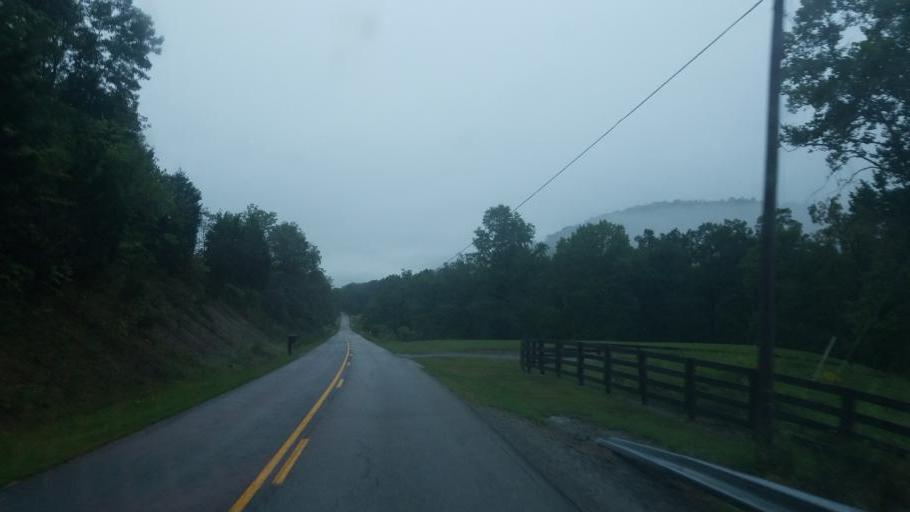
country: US
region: Kentucky
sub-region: Fleming County
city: Flemingsburg
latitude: 38.4063
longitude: -83.5874
